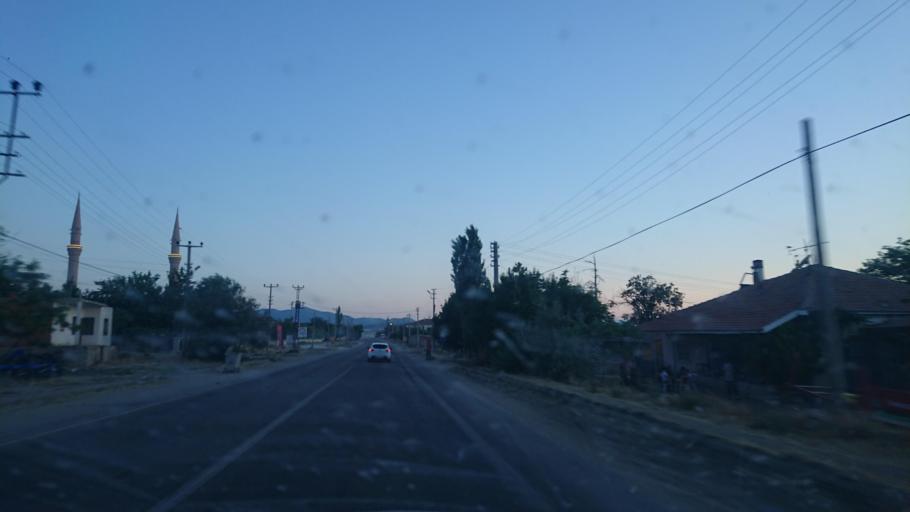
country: TR
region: Aksaray
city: Balci
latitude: 38.7919
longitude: 34.1237
